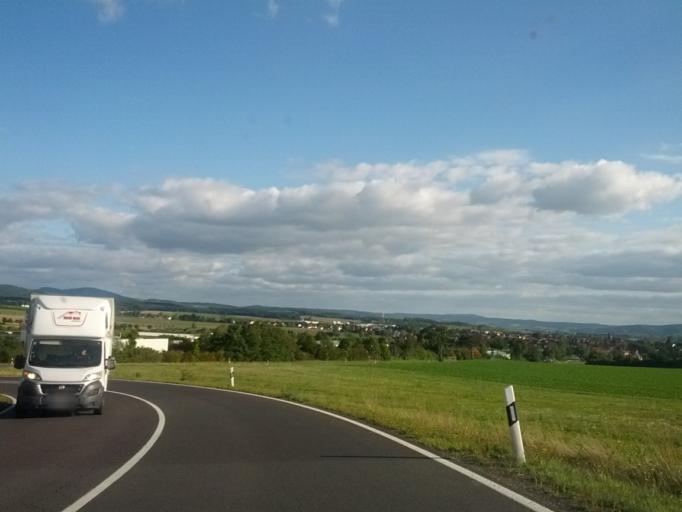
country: DE
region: Thuringia
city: Barchfeld
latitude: 50.8123
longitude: 10.2903
